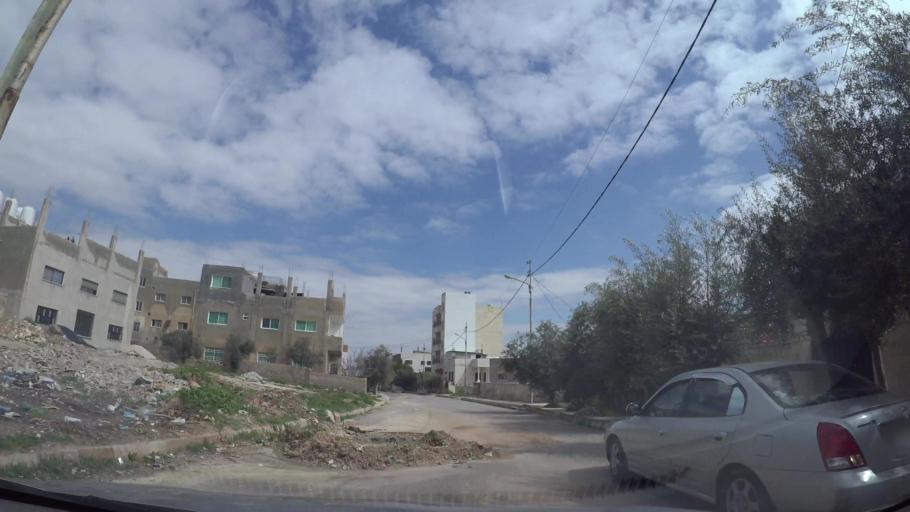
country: JO
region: Amman
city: Al Jubayhah
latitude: 32.0691
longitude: 35.8178
